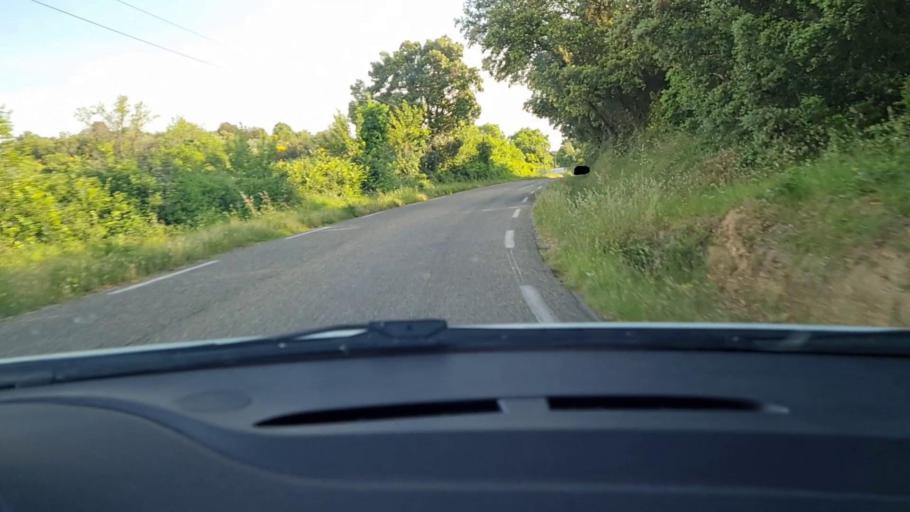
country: FR
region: Languedoc-Roussillon
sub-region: Departement du Gard
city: Bellegarde
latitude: 43.7635
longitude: 4.5099
